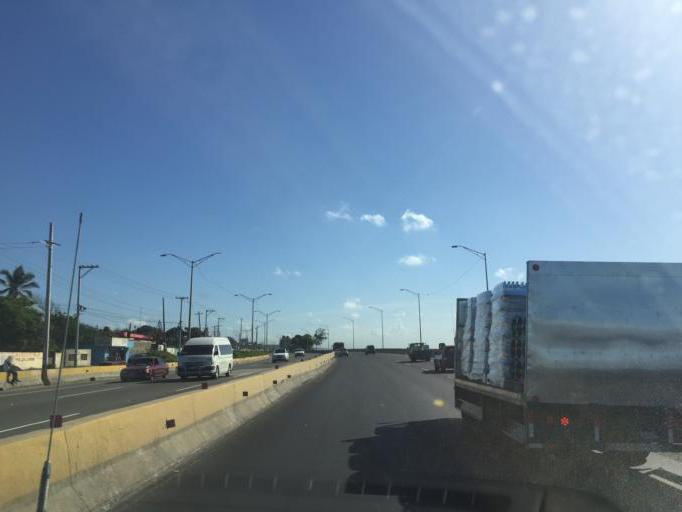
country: DO
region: Santo Domingo
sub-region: Santo Domingo
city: Santo Domingo Este
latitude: 18.4645
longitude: -69.8107
